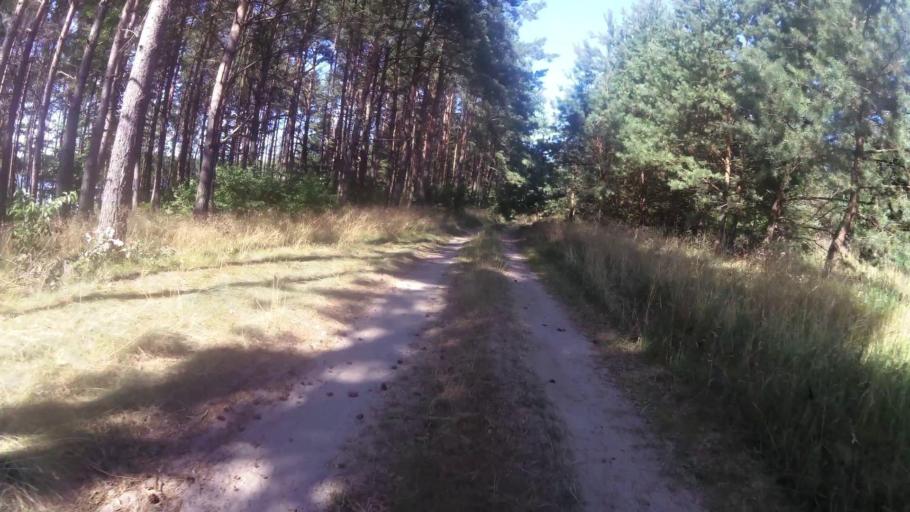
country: PL
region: West Pomeranian Voivodeship
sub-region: Powiat stargardzki
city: Insko
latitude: 53.4427
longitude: 15.6210
